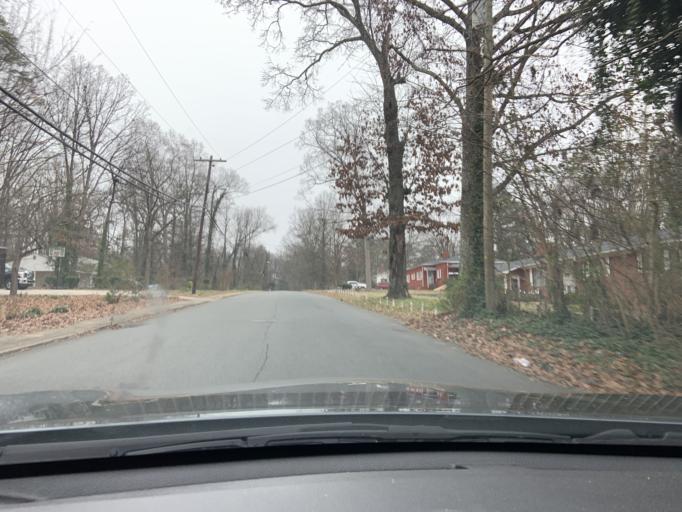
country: US
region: North Carolina
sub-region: Mecklenburg County
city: Charlotte
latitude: 35.2292
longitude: -80.9102
